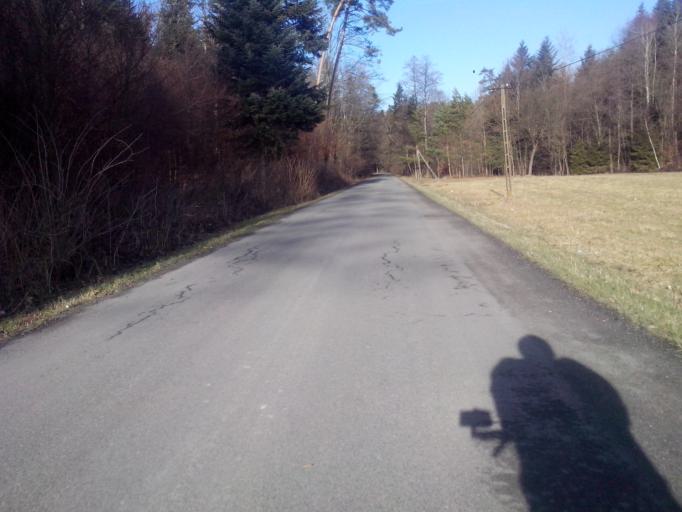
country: PL
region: Subcarpathian Voivodeship
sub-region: Powiat strzyzowski
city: Strzyzow
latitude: 49.8035
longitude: 21.8282
